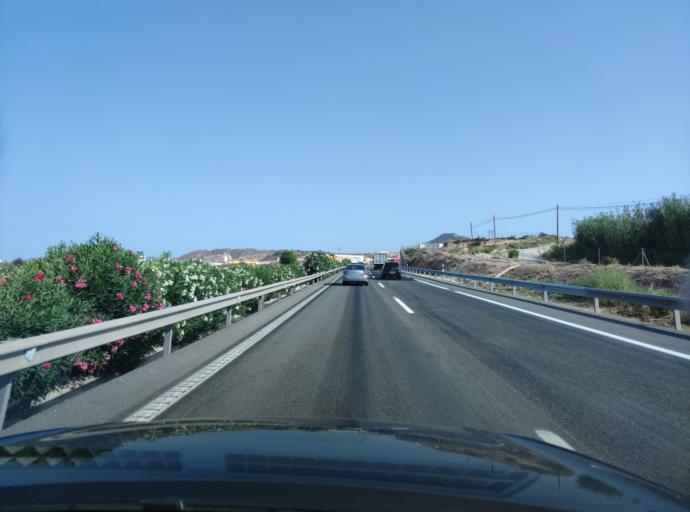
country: ES
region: Valencia
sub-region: Provincia de Alicante
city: Novelda
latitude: 38.4130
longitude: -0.7799
